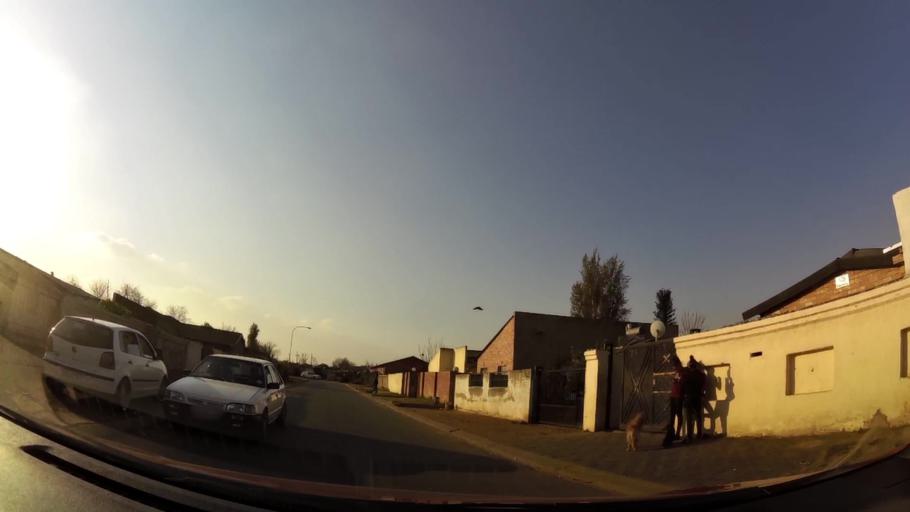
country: ZA
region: Gauteng
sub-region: City of Johannesburg Metropolitan Municipality
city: Soweto
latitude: -26.2908
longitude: 27.8949
